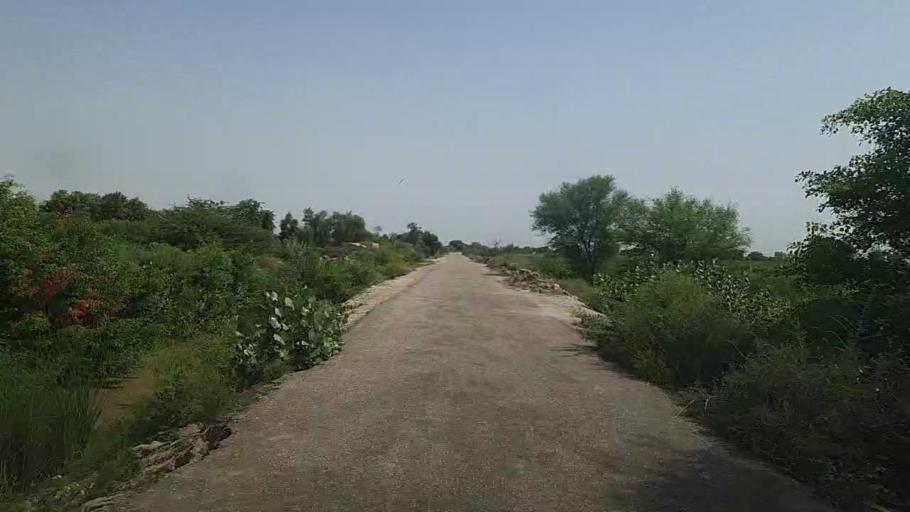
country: PK
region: Sindh
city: Pad Idan
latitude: 26.8054
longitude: 68.3324
